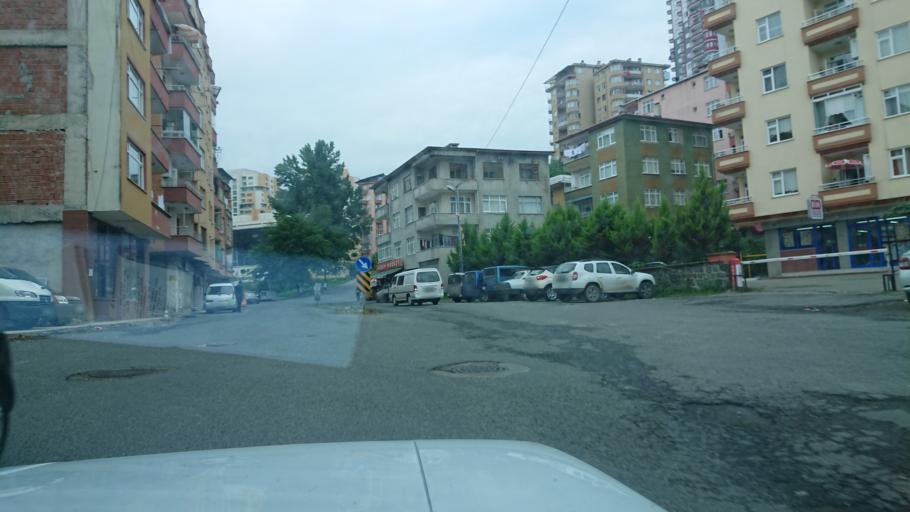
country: TR
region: Rize
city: Rize
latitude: 41.0189
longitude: 40.5163
